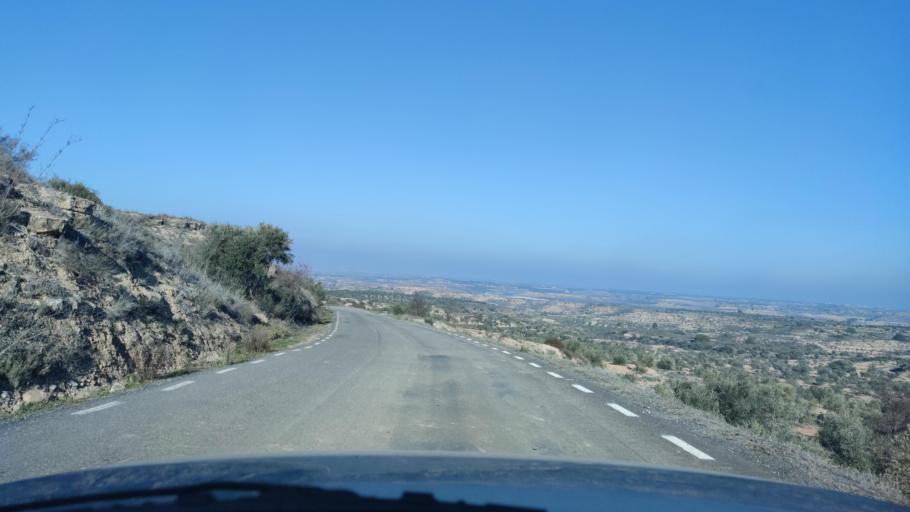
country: ES
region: Catalonia
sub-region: Provincia de Lleida
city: Torrebesses
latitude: 41.4429
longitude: 0.5586
